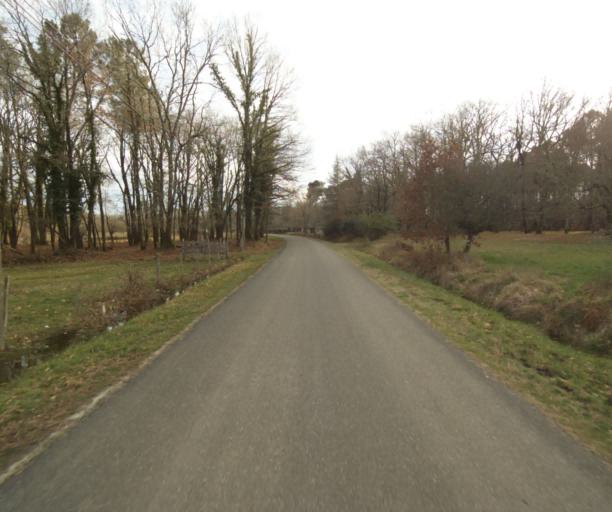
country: FR
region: Aquitaine
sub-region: Departement des Landes
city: Gabarret
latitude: 44.0246
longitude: 0.0476
